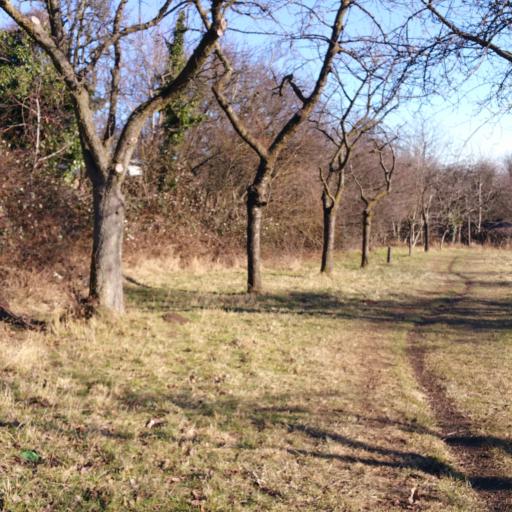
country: AT
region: Vienna
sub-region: Wien Stadt
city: Vienna
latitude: 48.2148
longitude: 16.2801
